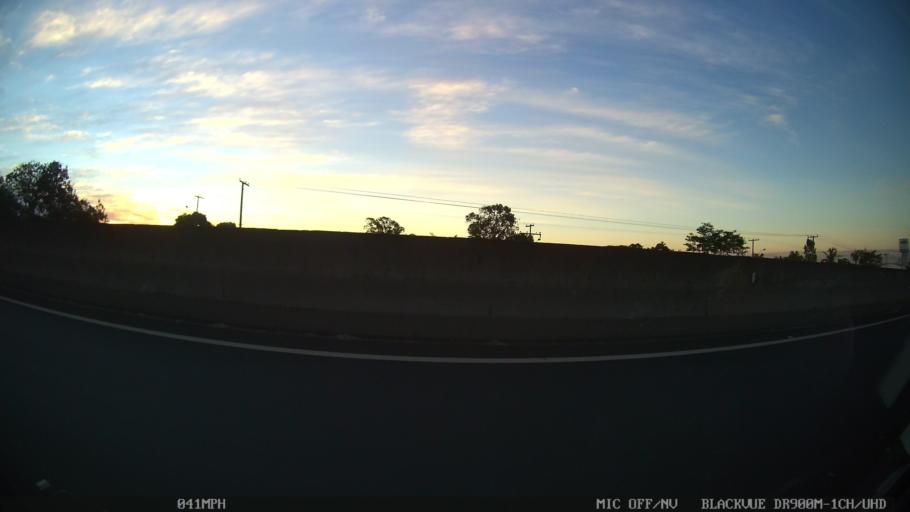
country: BR
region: Sao Paulo
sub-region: Catanduva
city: Catanduva
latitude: -21.1294
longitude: -49.0105
